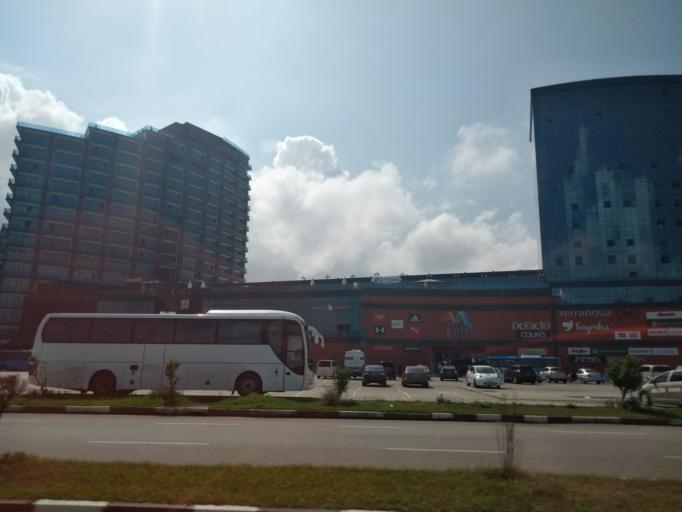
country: GE
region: Ajaria
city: Batumi
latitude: 41.6284
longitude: 41.6013
